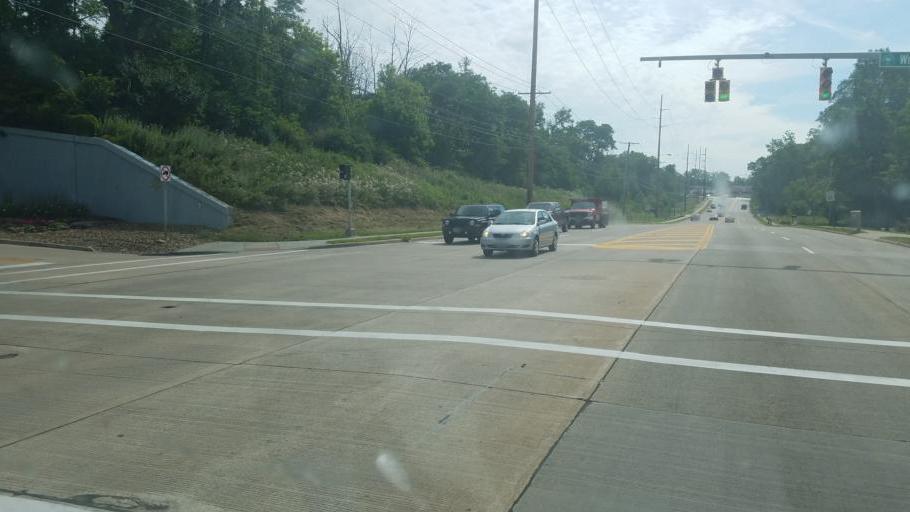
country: US
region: Ohio
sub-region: Cuyahoga County
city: Strongsville
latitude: 41.3133
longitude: -81.7912
